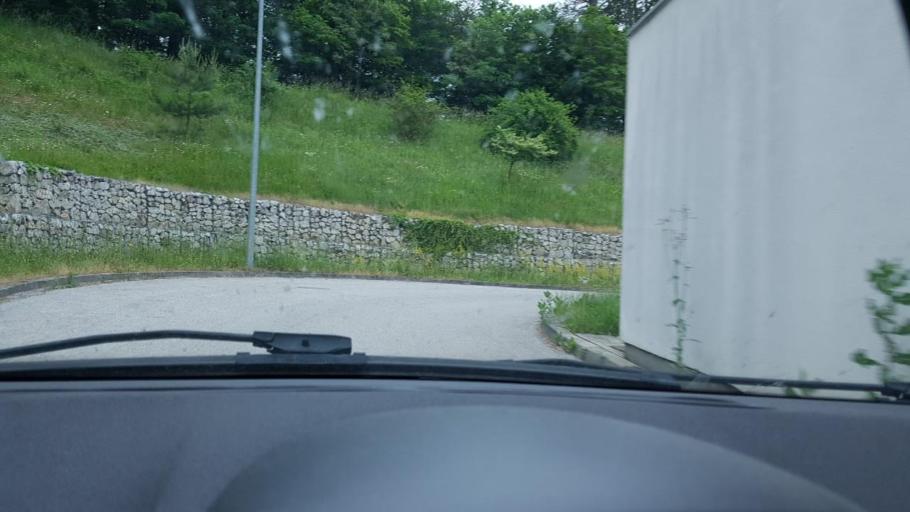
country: HR
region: Krapinsko-Zagorska
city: Zabok
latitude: 46.0181
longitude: 15.9381
